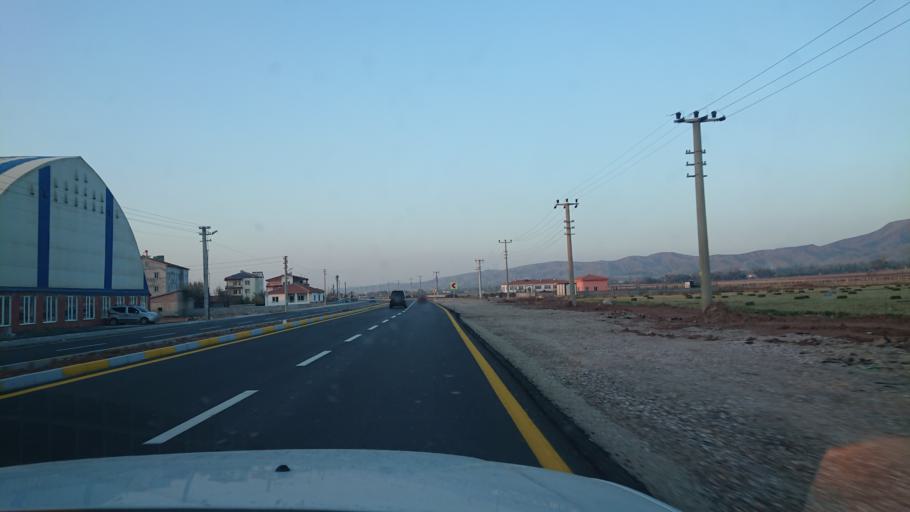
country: TR
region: Aksaray
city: Aksaray
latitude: 38.3233
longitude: 34.0527
